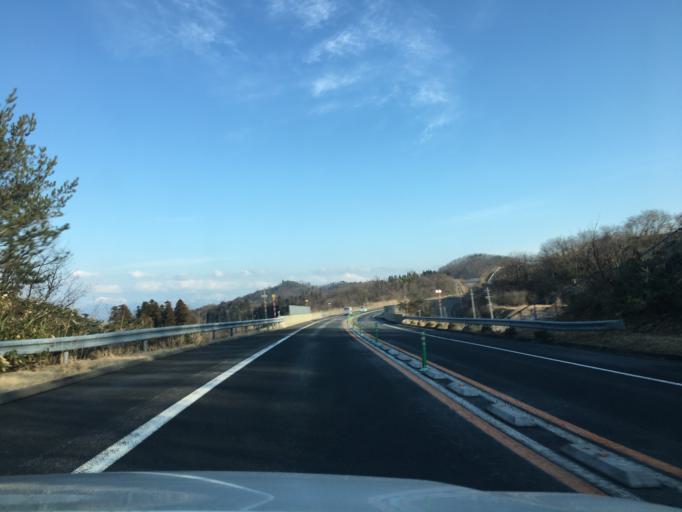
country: JP
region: Yamagata
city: Sagae
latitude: 38.4010
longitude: 140.2074
